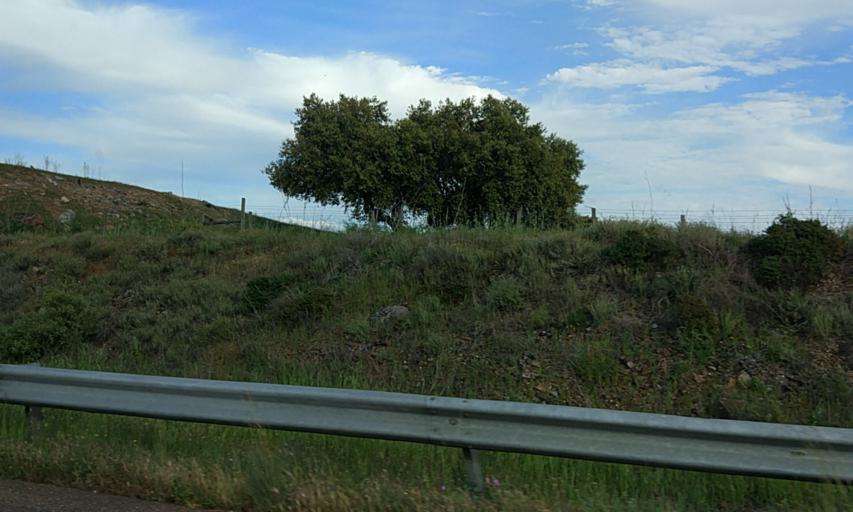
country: PT
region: Portalegre
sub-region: Elvas
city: Elvas
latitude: 38.8981
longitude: -7.2035
